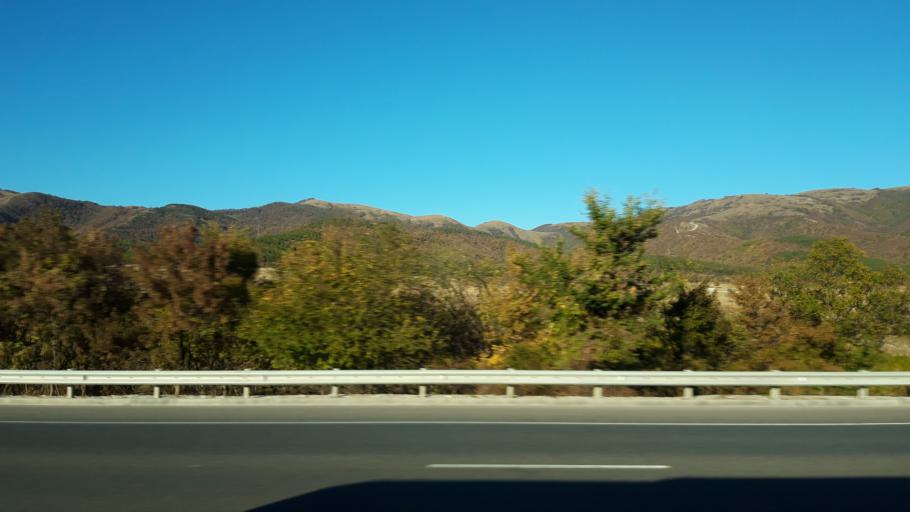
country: RU
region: Krasnodarskiy
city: Kabardinka
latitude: 44.6380
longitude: 37.9882
